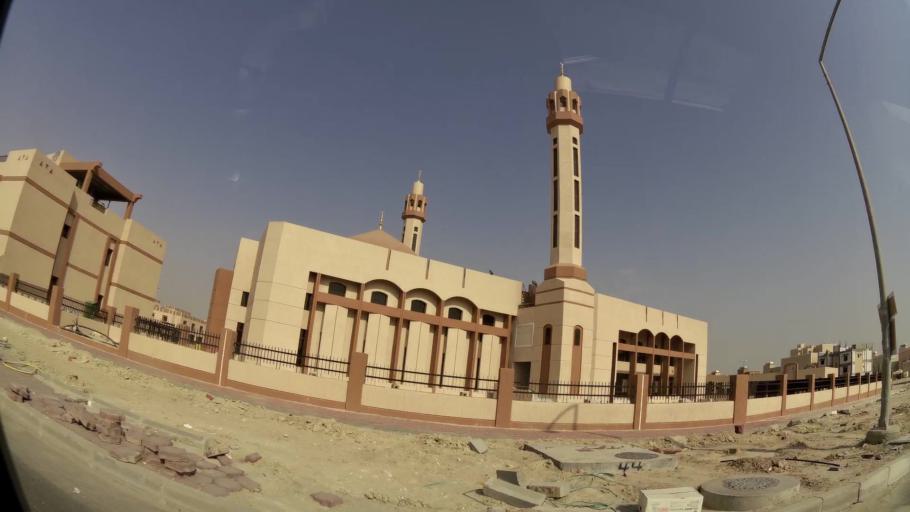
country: KW
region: Muhafazat al Jahra'
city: Al Jahra'
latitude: 29.3513
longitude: 47.7570
